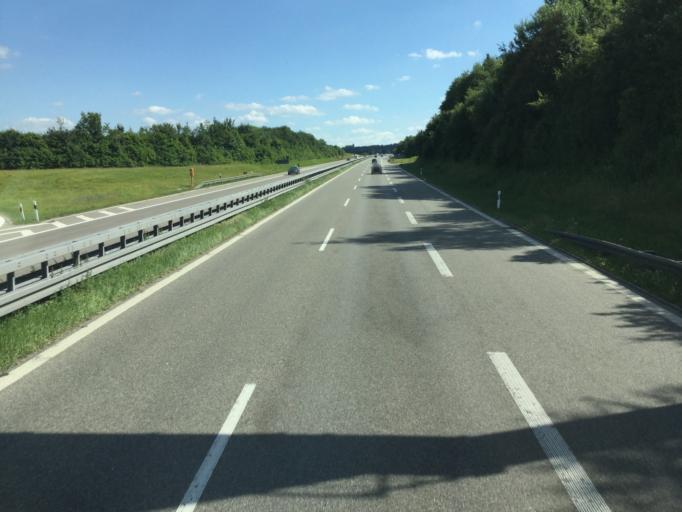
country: DE
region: Baden-Wuerttemberg
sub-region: Tuebingen Region
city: Leutkirch im Allgau
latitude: 47.8170
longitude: 9.9909
